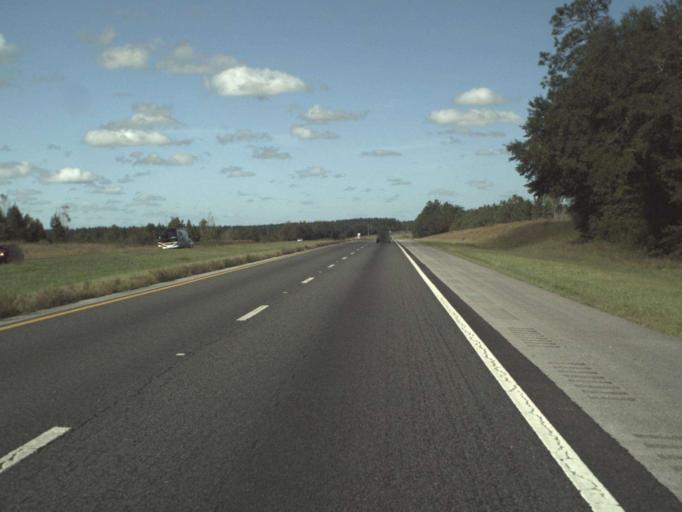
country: US
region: Florida
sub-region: Jackson County
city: Marianna
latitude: 30.6819
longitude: -85.0951
